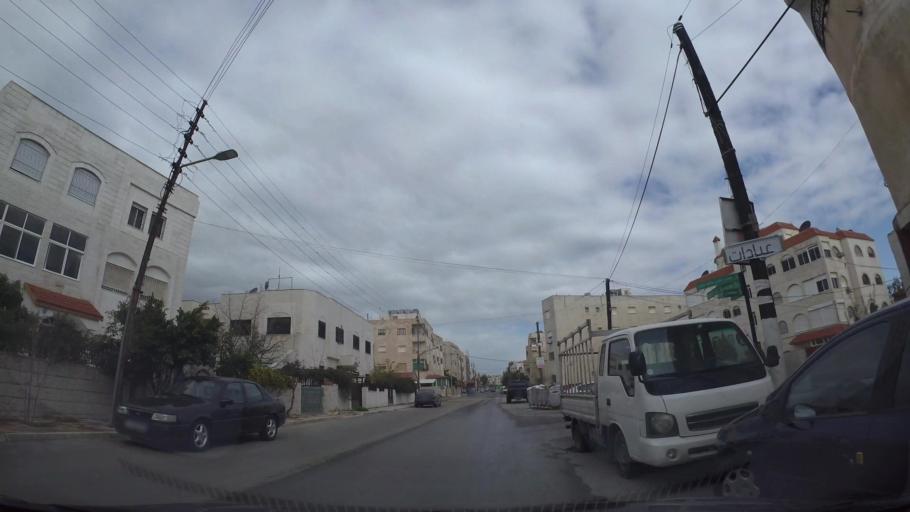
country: JO
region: Amman
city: Wadi as Sir
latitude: 31.9477
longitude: 35.8363
